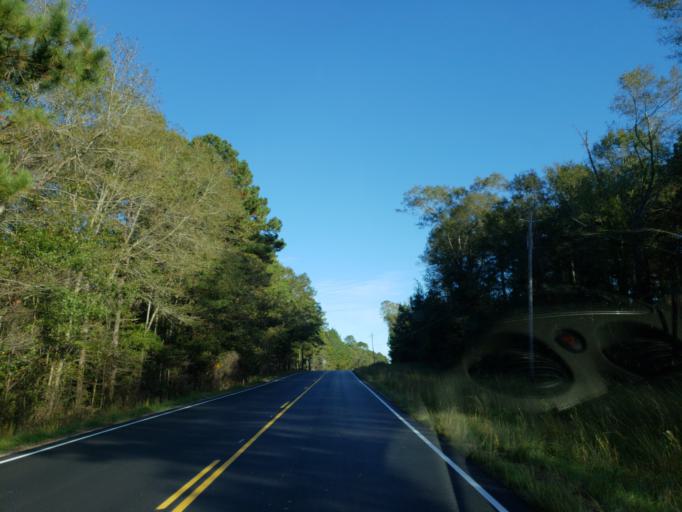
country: US
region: Mississippi
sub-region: Perry County
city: Richton
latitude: 31.3731
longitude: -88.8278
